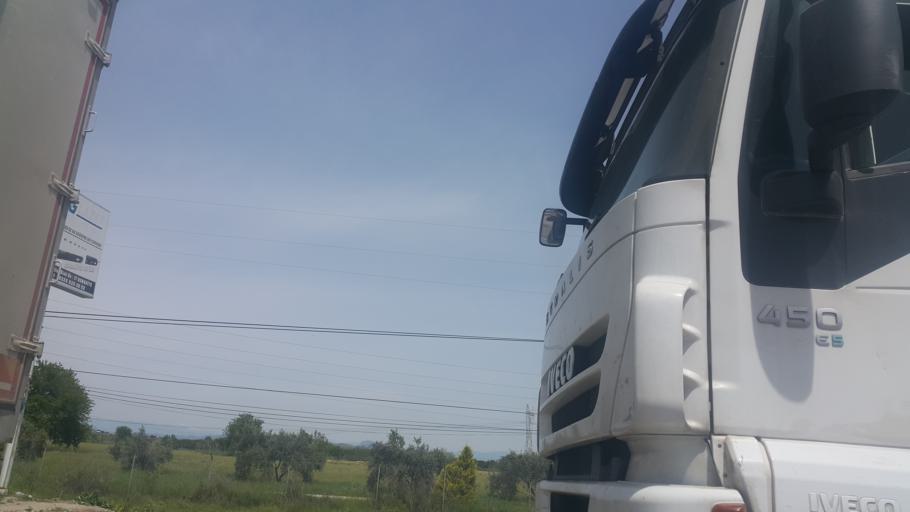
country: TR
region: Osmaniye
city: Toprakkale
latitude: 37.0608
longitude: 36.1139
